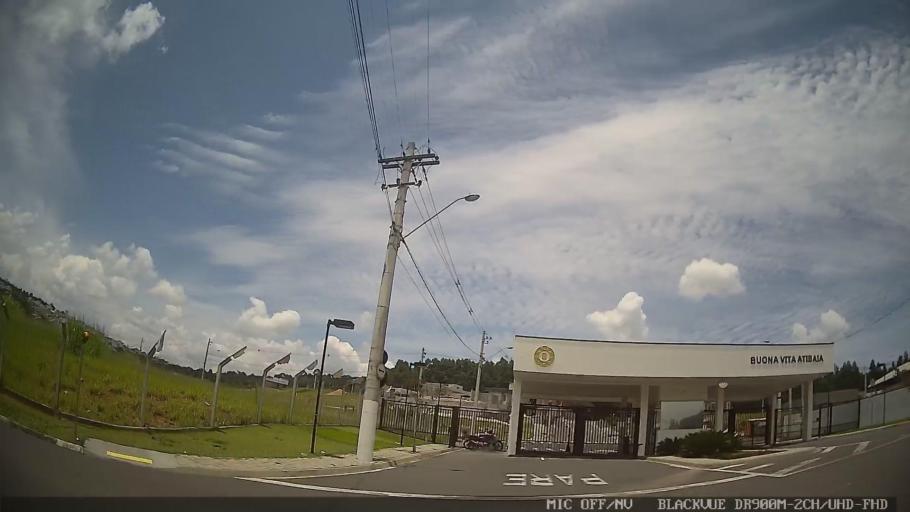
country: BR
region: Sao Paulo
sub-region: Atibaia
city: Atibaia
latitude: -23.0709
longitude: -46.6193
